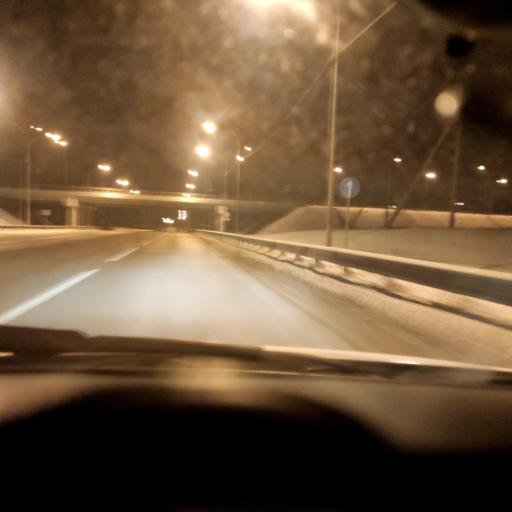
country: RU
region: Kursk
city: Fatezh
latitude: 52.0972
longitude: 35.8212
